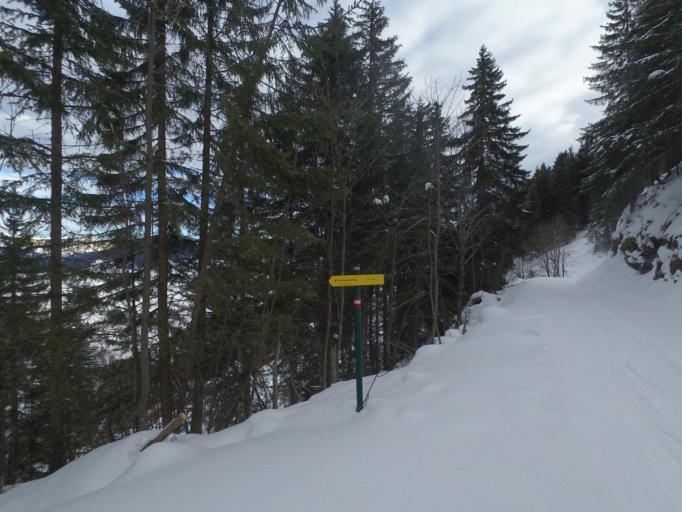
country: AT
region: Salzburg
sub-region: Politischer Bezirk Sankt Johann im Pongau
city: Sankt Johann im Pongau
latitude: 47.3161
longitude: 13.2230
